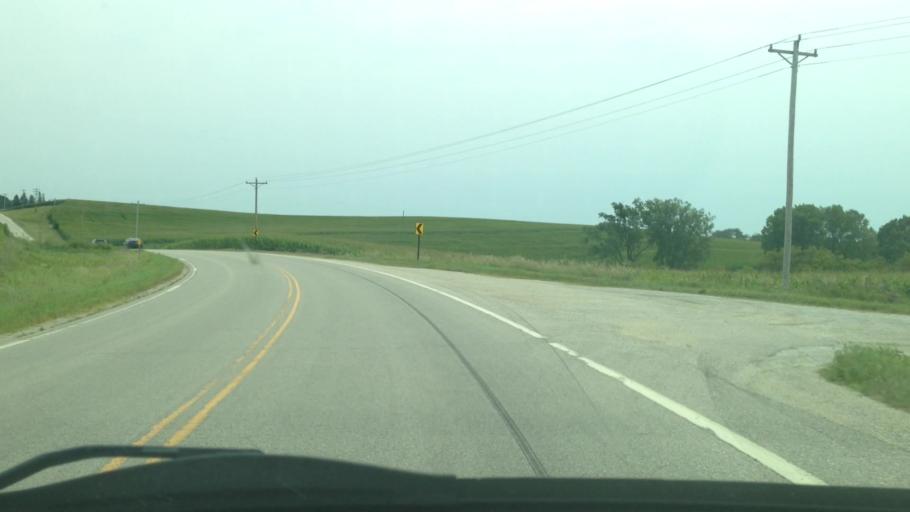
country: US
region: Minnesota
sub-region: Fillmore County
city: Preston
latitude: 43.7279
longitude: -91.9979
